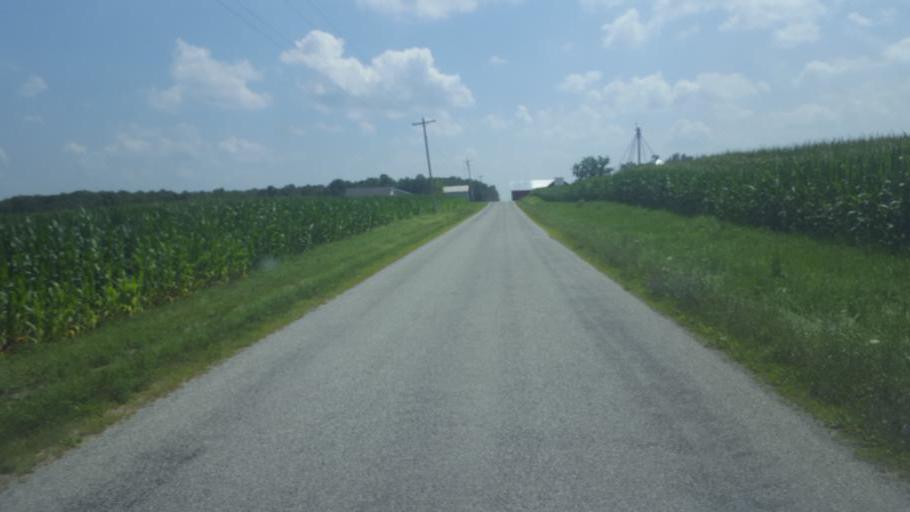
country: US
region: Ohio
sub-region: Richland County
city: Lexington
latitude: 40.6264
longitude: -82.6902
